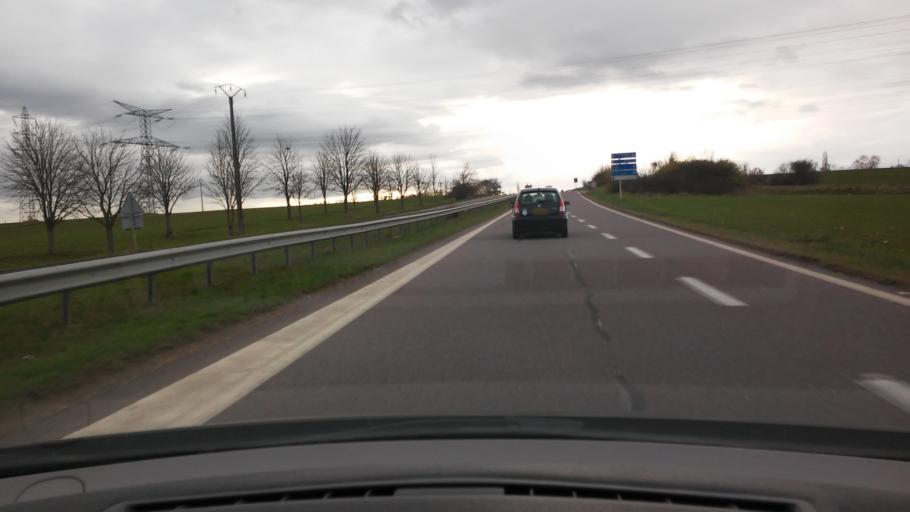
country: FR
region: Lorraine
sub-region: Departement de la Moselle
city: Argancy
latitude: 49.2023
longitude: 6.2088
